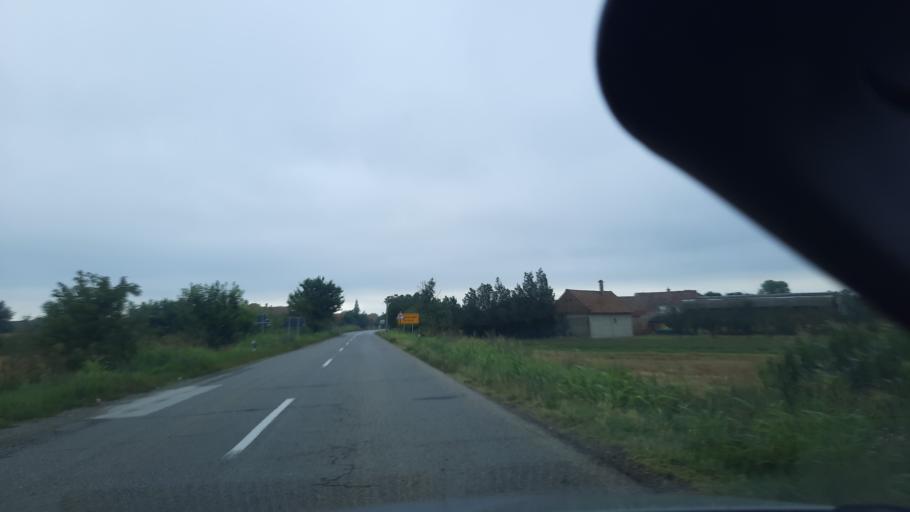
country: RS
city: Farkazdin
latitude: 45.1916
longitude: 20.4651
